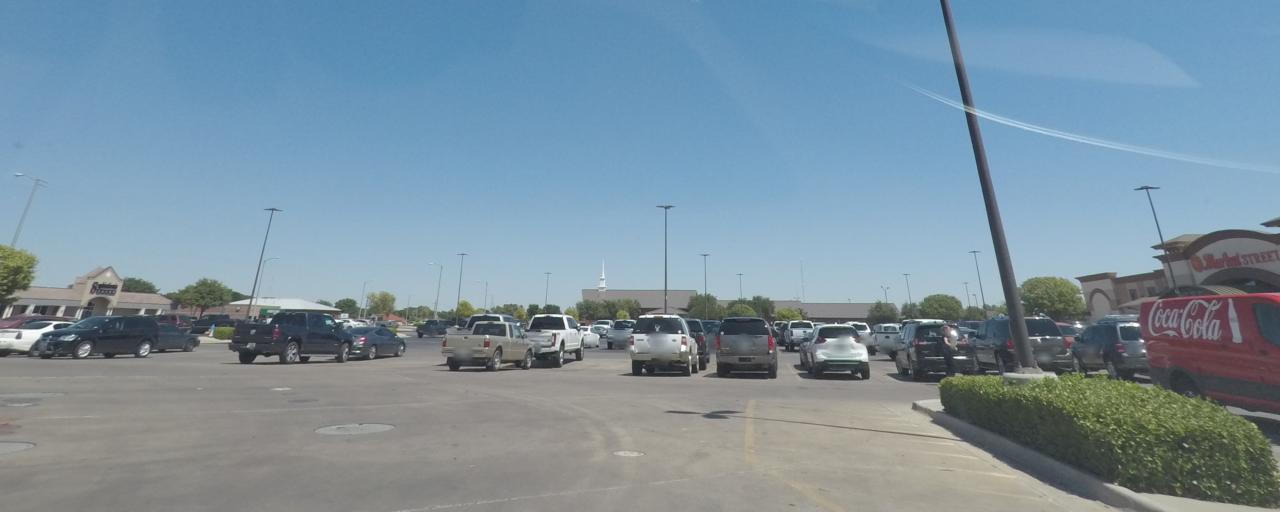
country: US
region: Texas
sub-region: Lubbock County
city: Lubbock
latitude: 33.5039
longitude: -101.9036
